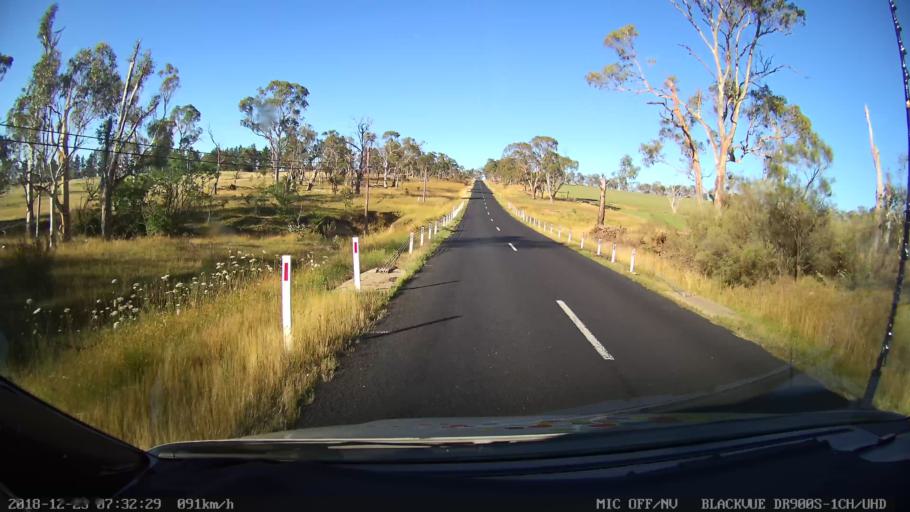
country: AU
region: New South Wales
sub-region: Armidale Dumaresq
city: Enmore
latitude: -30.5050
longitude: 152.1163
